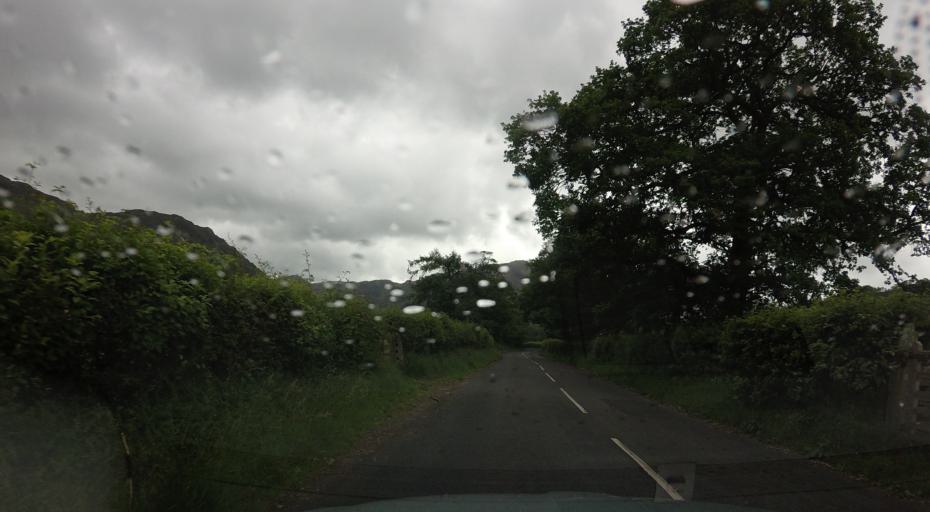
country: GB
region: England
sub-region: Cumbria
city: Keswick
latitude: 54.5290
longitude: -3.1515
